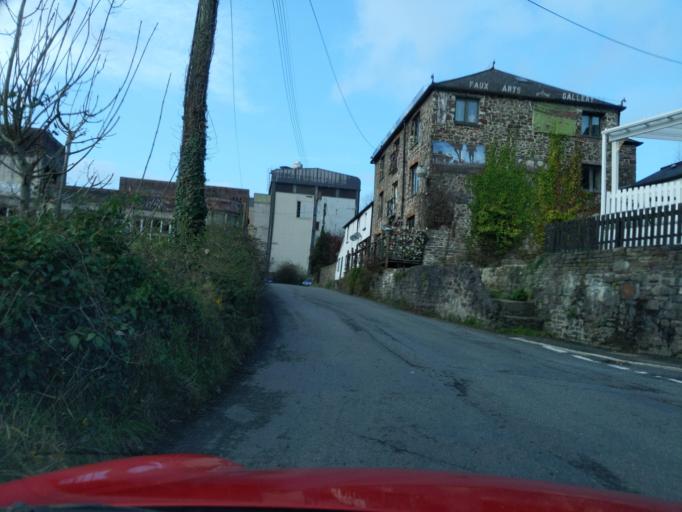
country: GB
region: England
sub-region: Devon
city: Great Torrington
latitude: 50.9488
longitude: -4.1544
